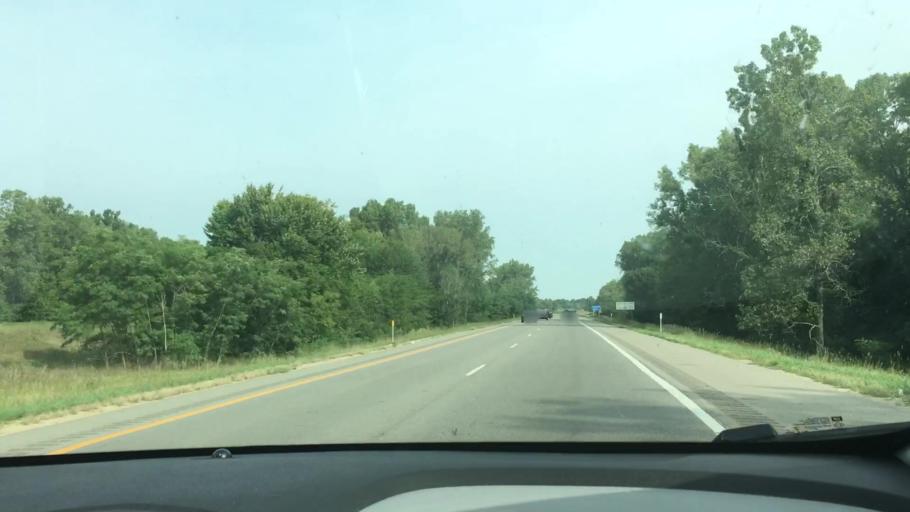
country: US
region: Michigan
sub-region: Kalamazoo County
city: Schoolcraft
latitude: 42.1490
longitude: -85.6390
